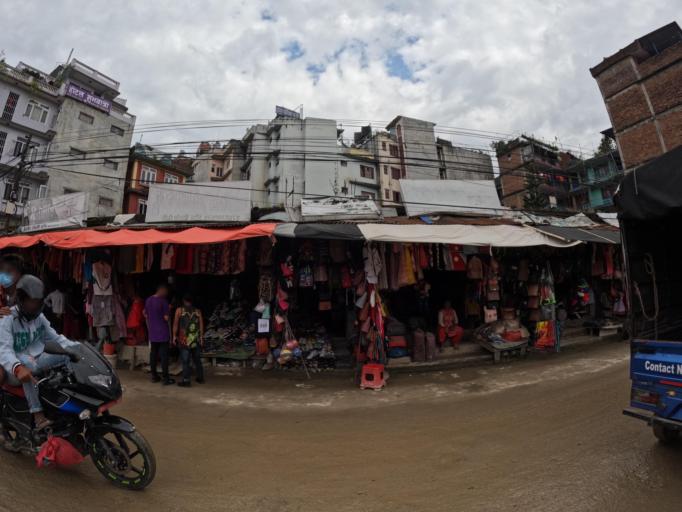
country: NP
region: Central Region
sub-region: Bagmati Zone
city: Kathmandu
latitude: 27.7360
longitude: 85.3076
